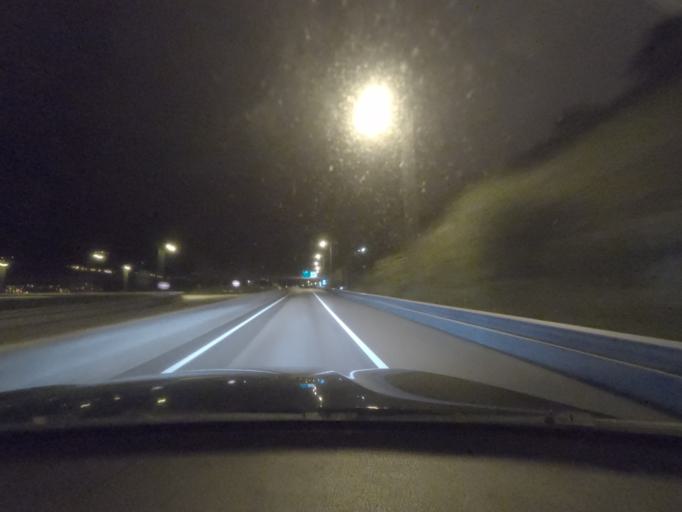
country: PT
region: Vila Real
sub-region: Vila Real
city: Vila Real
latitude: 41.3006
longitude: -7.7533
